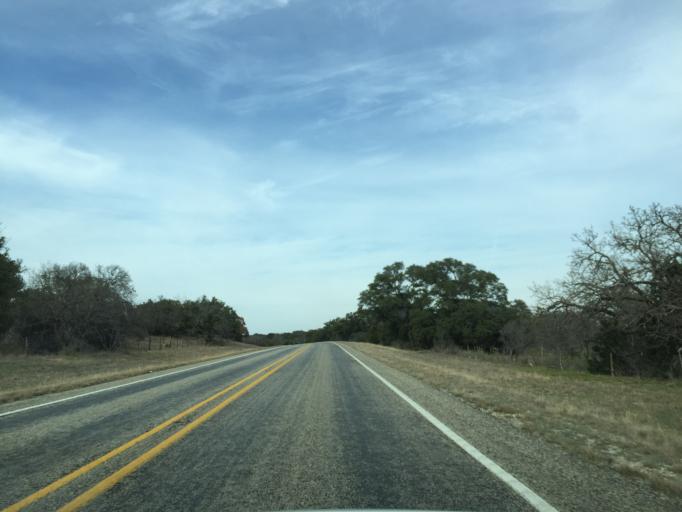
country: US
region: Texas
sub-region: Gillespie County
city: Fredericksburg
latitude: 30.4886
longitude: -98.7036
